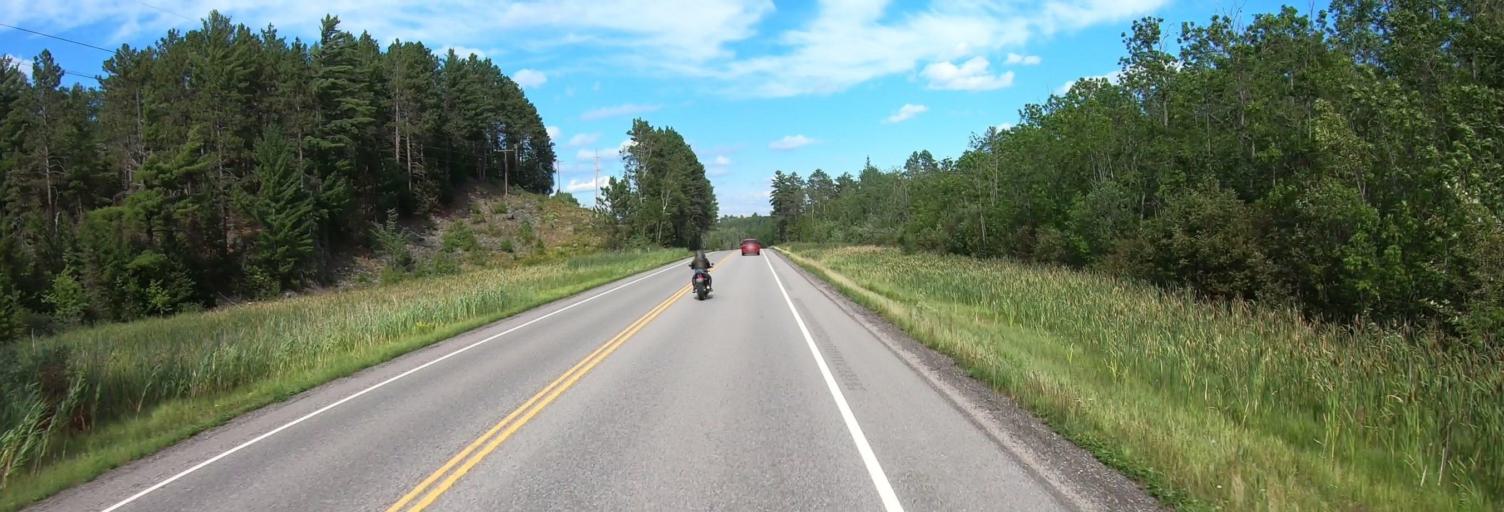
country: US
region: Minnesota
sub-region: Saint Louis County
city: Ely
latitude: 47.8749
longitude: -92.0201
